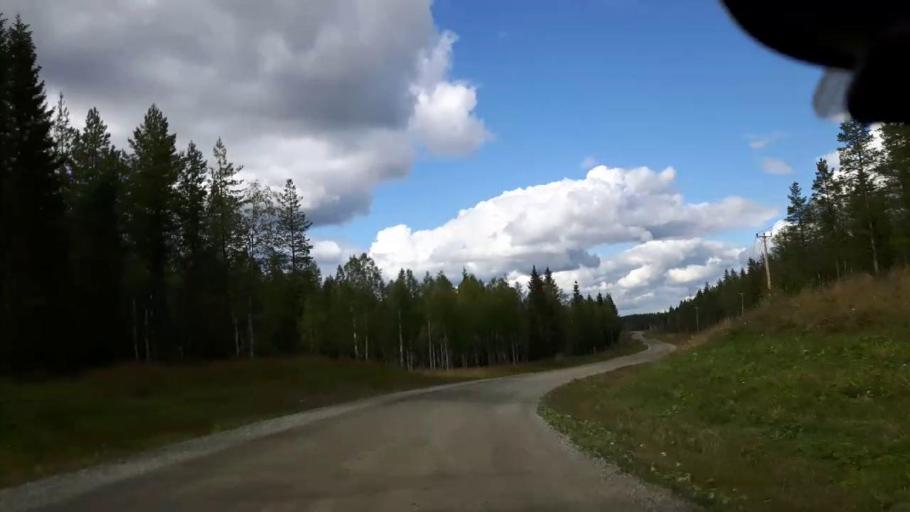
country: SE
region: Jaemtland
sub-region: Stroemsunds Kommun
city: Stroemsund
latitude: 63.3747
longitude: 15.5628
